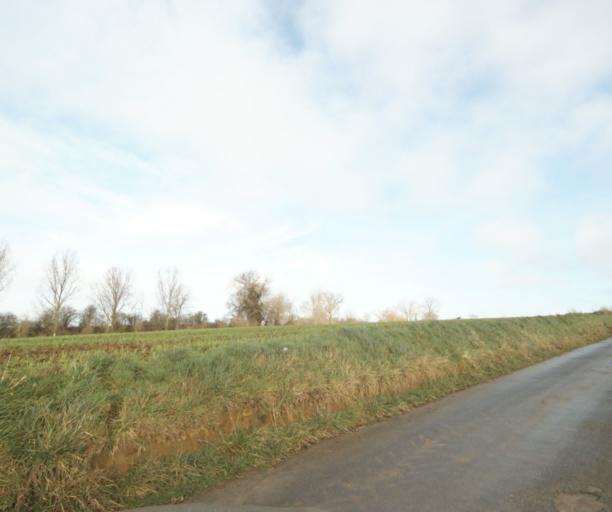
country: FR
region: Nord-Pas-de-Calais
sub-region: Departement du Nord
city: Vendegies-sur-Ecaillon
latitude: 50.2745
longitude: 3.4849
